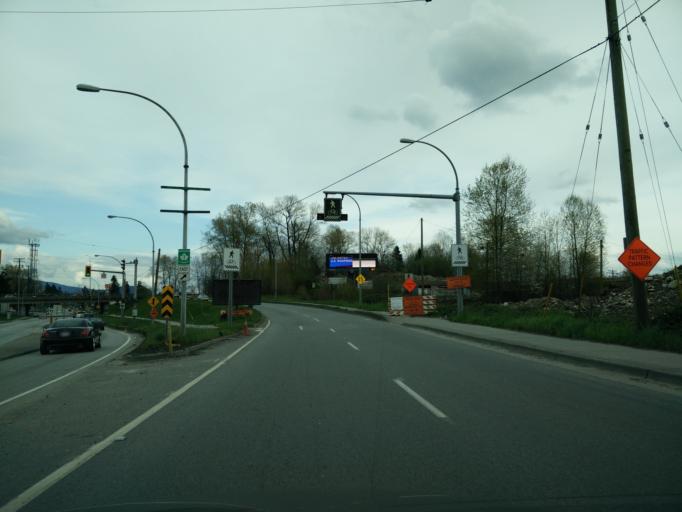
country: CA
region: British Columbia
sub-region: Fraser Valley Regional District
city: North Vancouver
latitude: 49.3047
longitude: -123.0304
